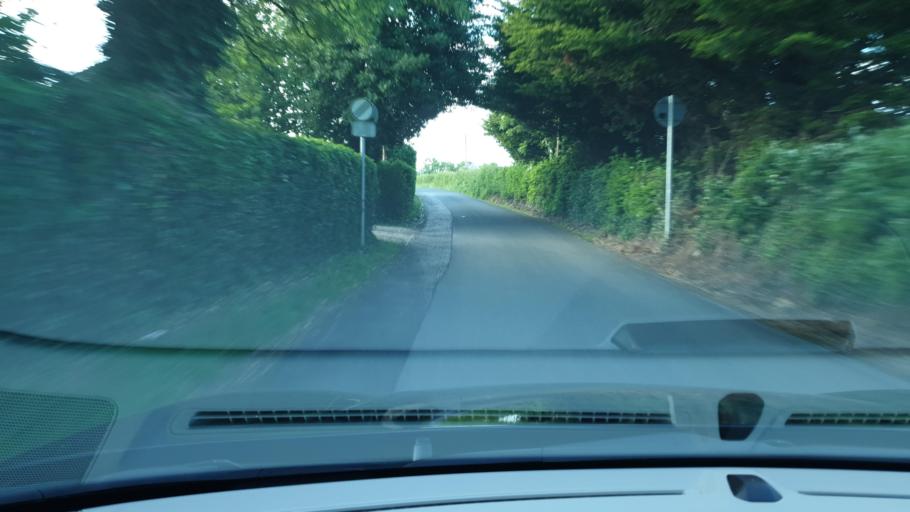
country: IE
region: Leinster
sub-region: An Mhi
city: Ashbourne
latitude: 53.5121
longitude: -6.3845
